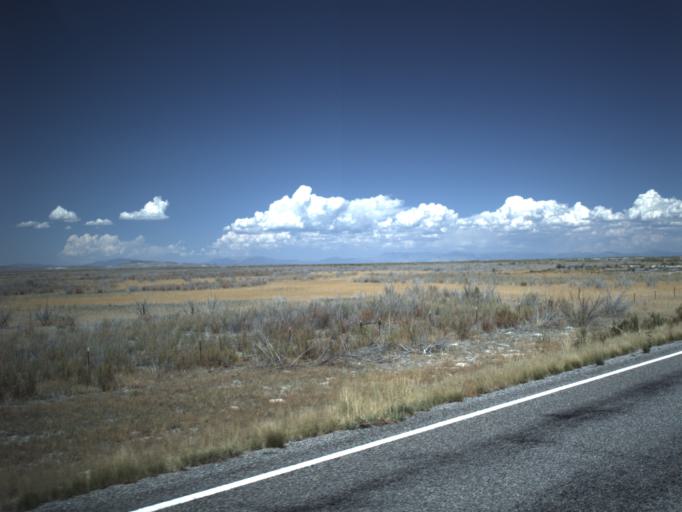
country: US
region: Utah
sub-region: Millard County
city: Delta
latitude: 39.2660
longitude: -112.8705
